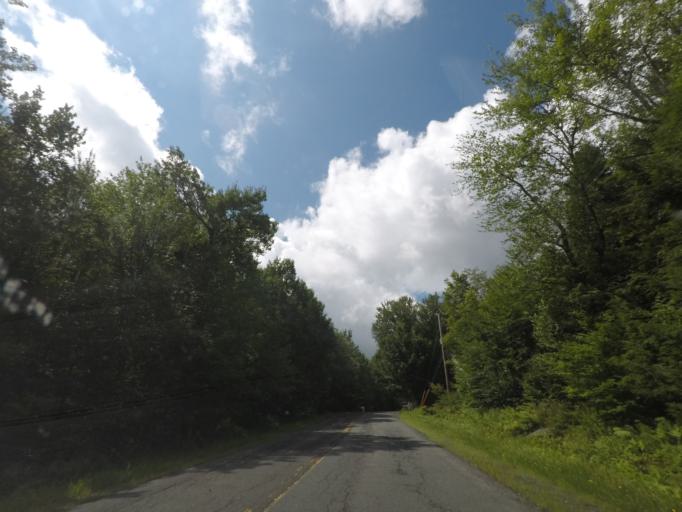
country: US
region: New York
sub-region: Rensselaer County
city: Averill Park
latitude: 42.6389
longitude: -73.4401
